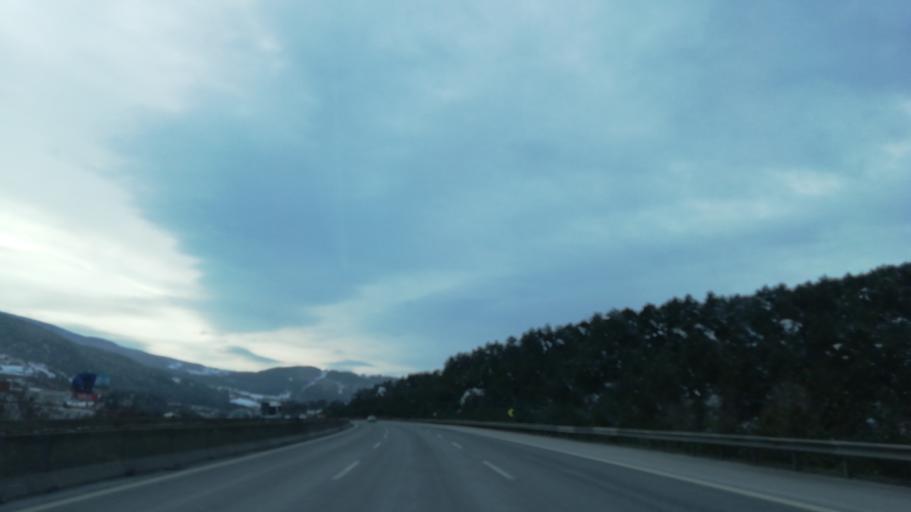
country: TR
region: Bolu
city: Gokcesu
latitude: 40.7394
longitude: 31.8250
